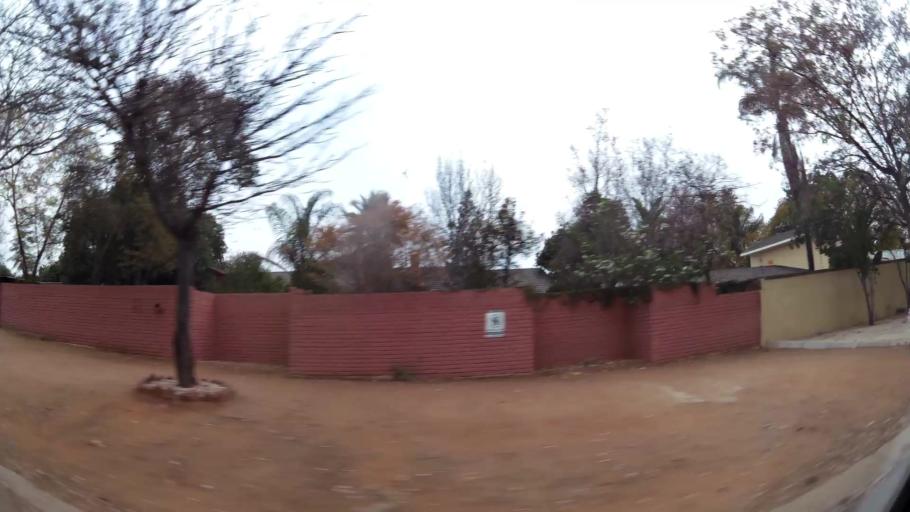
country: ZA
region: Limpopo
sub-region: Capricorn District Municipality
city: Polokwane
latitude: -23.9013
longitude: 29.4691
